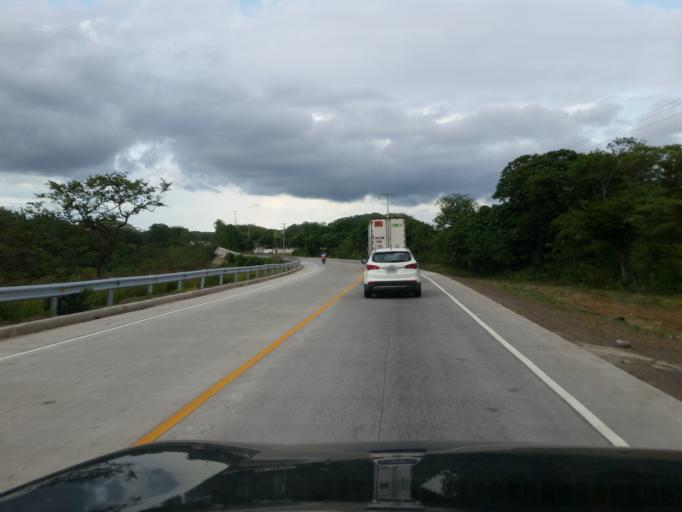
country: NI
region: Managua
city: Ciudad Sandino
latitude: 12.0778
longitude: -86.4252
